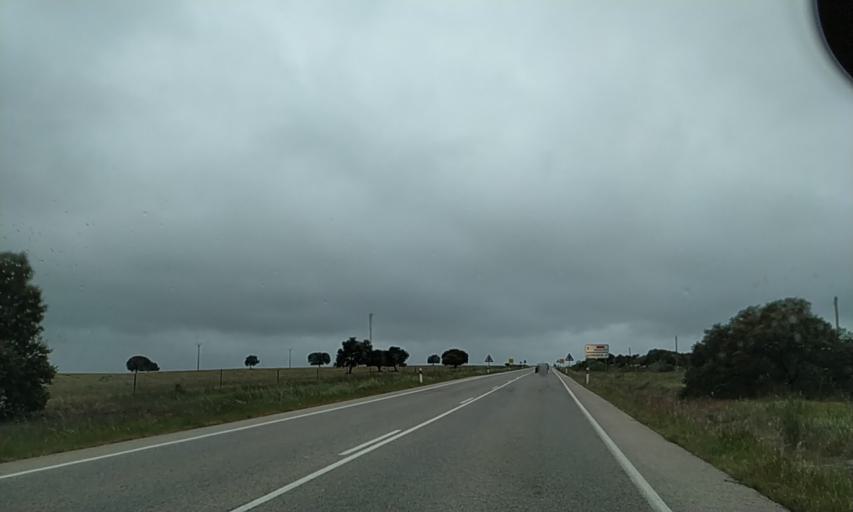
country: ES
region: Extremadura
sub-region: Provincia de Caceres
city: Malpartida de Caceres
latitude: 39.3669
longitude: -6.4588
